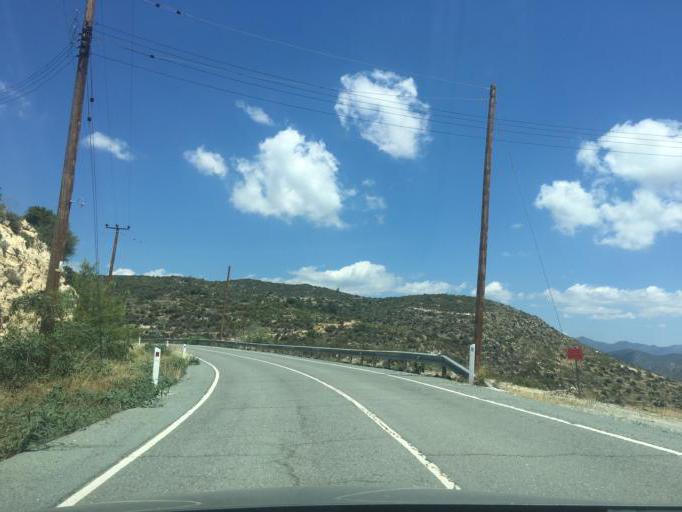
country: CY
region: Limassol
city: Mouttagiaka
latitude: 34.7540
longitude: 33.0587
